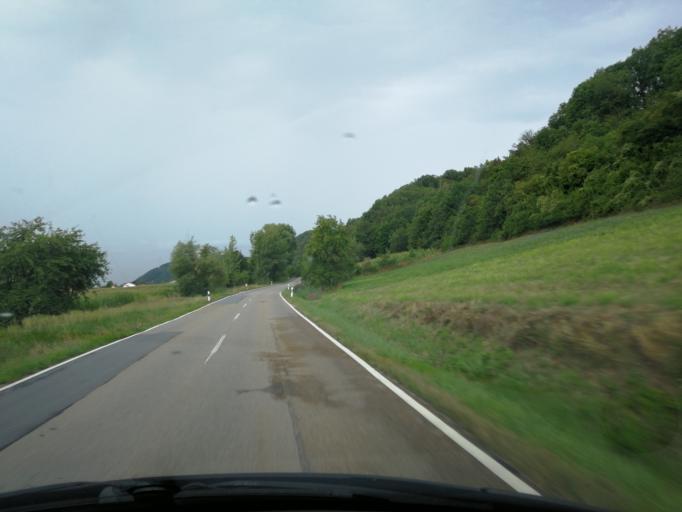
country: DE
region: Bavaria
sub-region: Upper Palatinate
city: Wiesent
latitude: 49.0183
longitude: 12.3217
